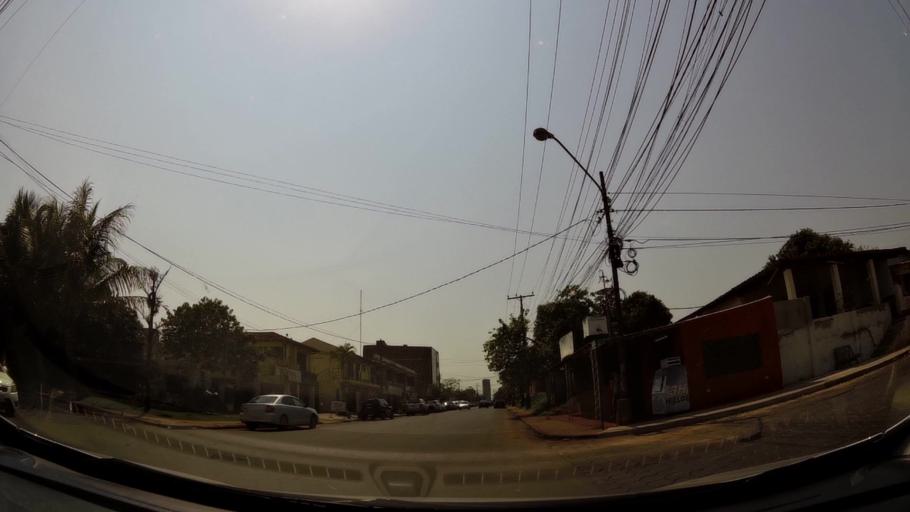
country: PY
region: Alto Parana
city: Presidente Franco
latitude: -25.5251
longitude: -54.6203
